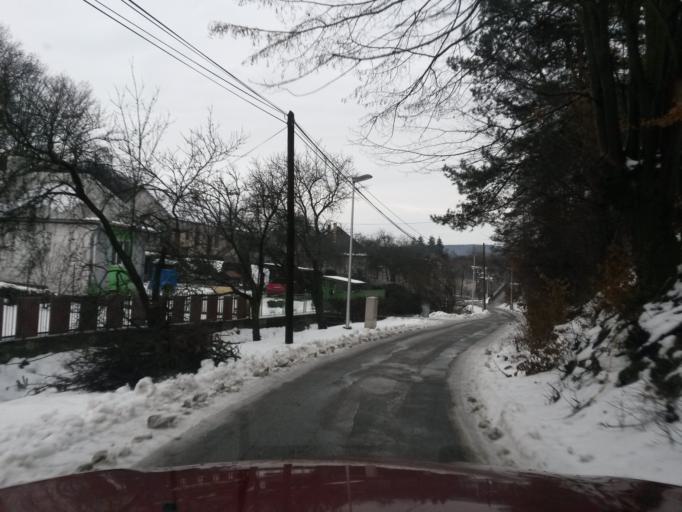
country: SK
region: Kosicky
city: Kosice
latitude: 48.7935
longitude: 21.2360
